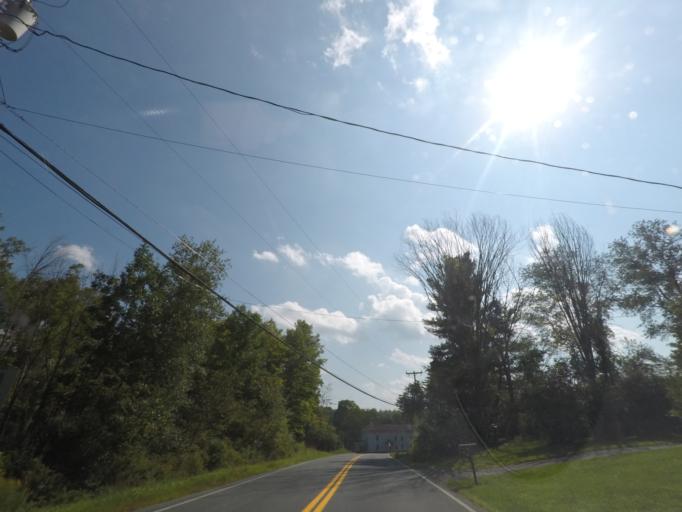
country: US
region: New York
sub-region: Rensselaer County
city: Poestenkill
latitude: 42.6867
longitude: -73.5256
